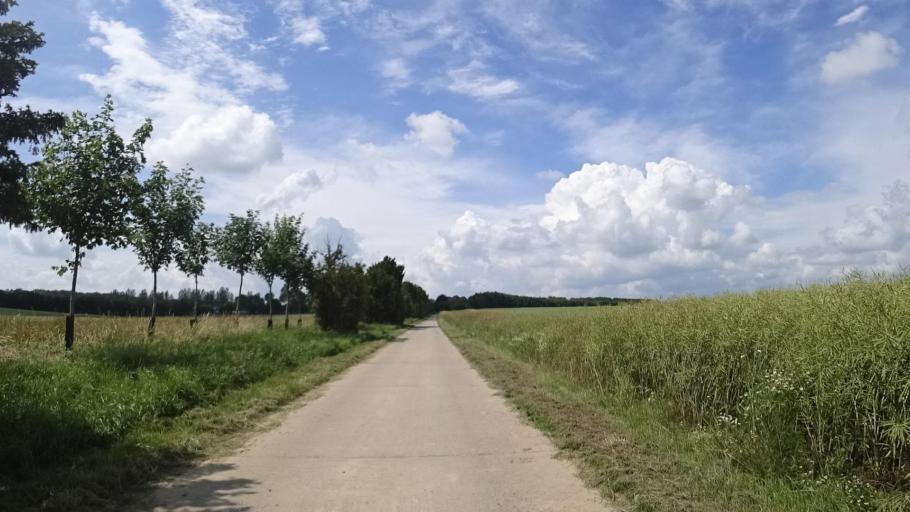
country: BE
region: Wallonia
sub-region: Province du Brabant Wallon
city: Perwez
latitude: 50.6107
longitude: 4.7679
